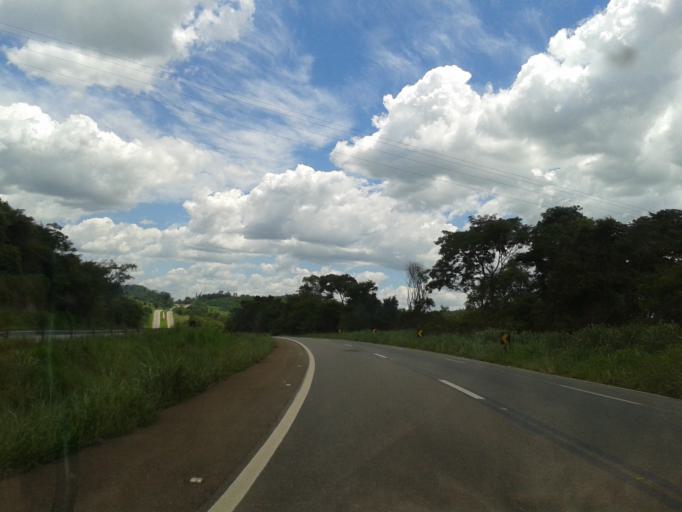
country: BR
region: Goias
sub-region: Neropolis
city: Neropolis
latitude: -16.2985
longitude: -49.2769
